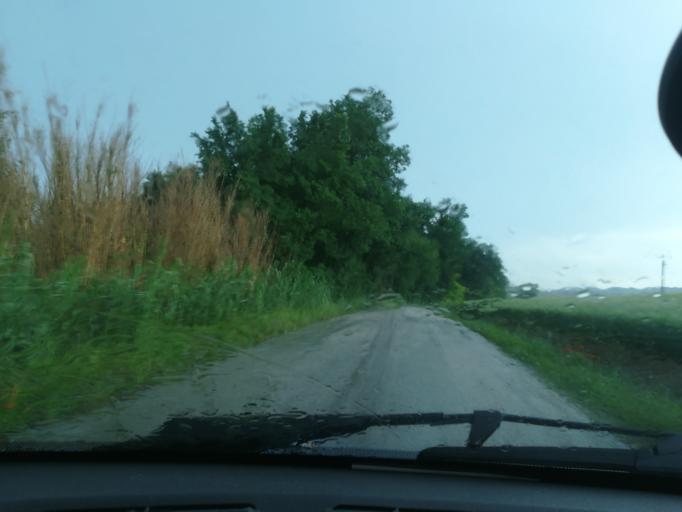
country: IT
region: The Marches
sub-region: Provincia di Macerata
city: Passo di Treia
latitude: 43.3021
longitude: 13.3447
